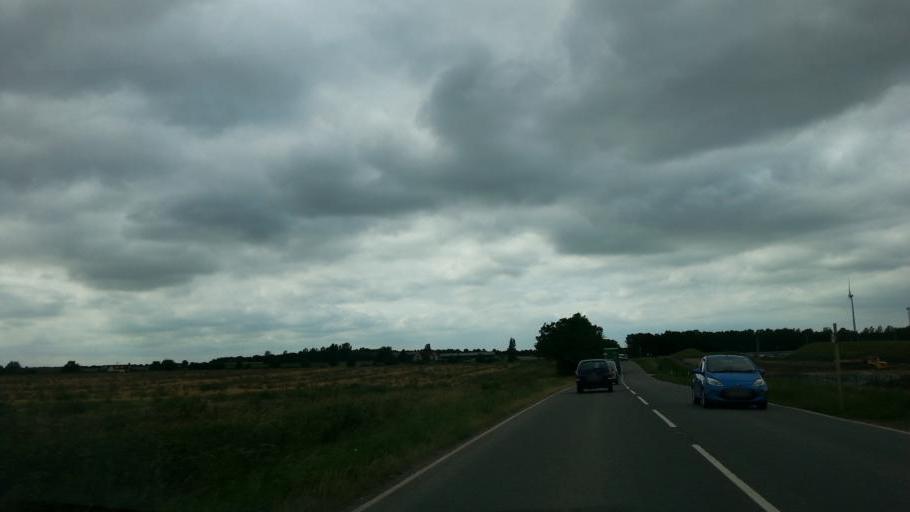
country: GB
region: England
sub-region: Cambridgeshire
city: Godmanchester
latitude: 52.2919
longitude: -0.1494
